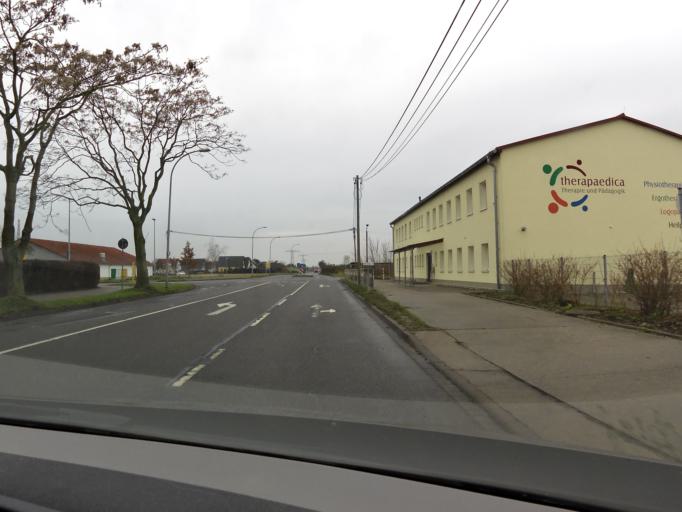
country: DE
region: Saxony
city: Schkeuditz
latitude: 51.3583
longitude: 12.2819
